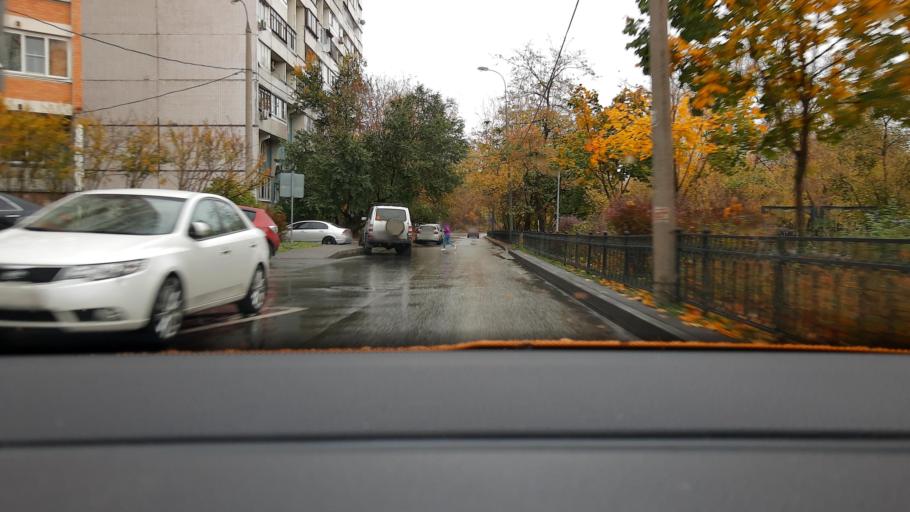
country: RU
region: Moscow
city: Strogino
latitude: 55.8170
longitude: 37.4015
